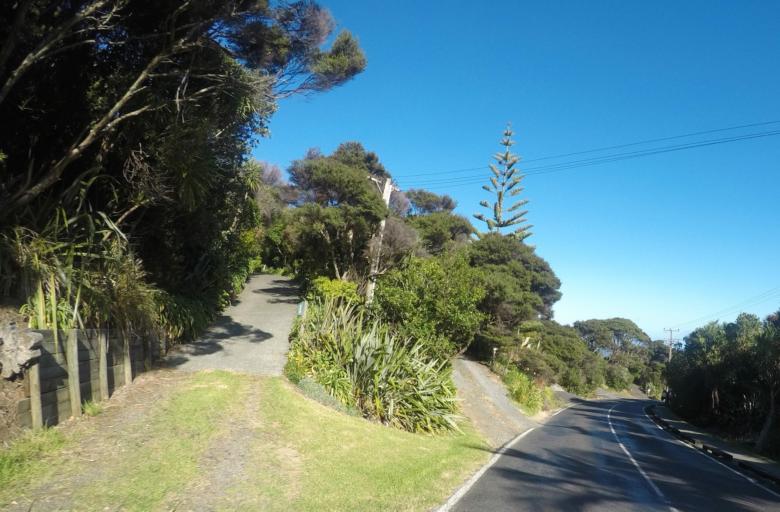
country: NZ
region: Auckland
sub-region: Auckland
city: Muriwai Beach
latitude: -36.9575
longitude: 174.4781
